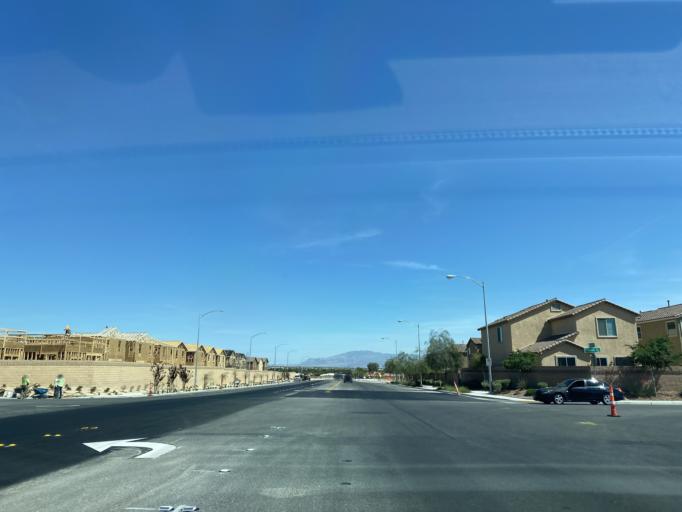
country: US
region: Nevada
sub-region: Clark County
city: Spring Valley
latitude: 36.0809
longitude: -115.2608
